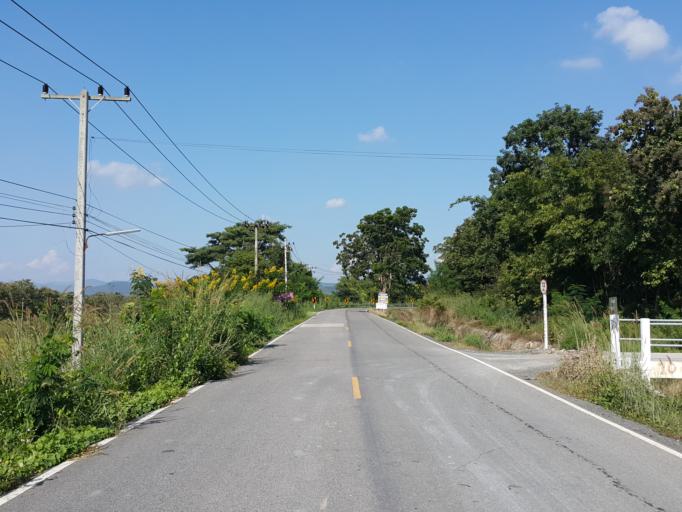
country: TH
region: Chiang Mai
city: San Kamphaeng
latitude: 18.7736
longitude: 99.1742
